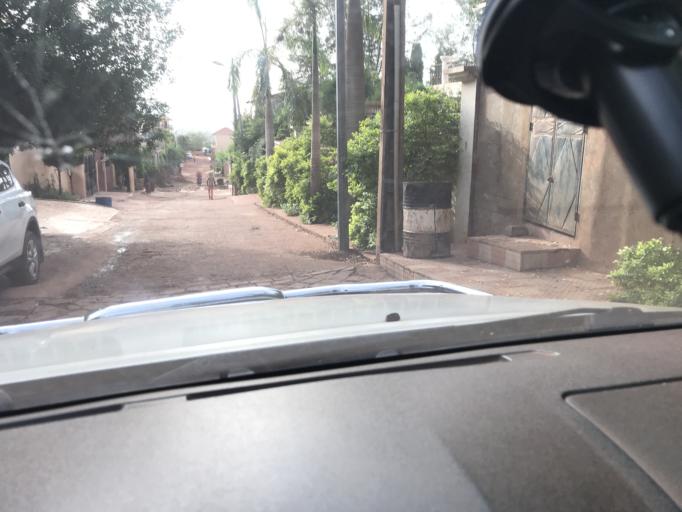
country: ML
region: Bamako
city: Bamako
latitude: 12.5882
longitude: -8.0066
